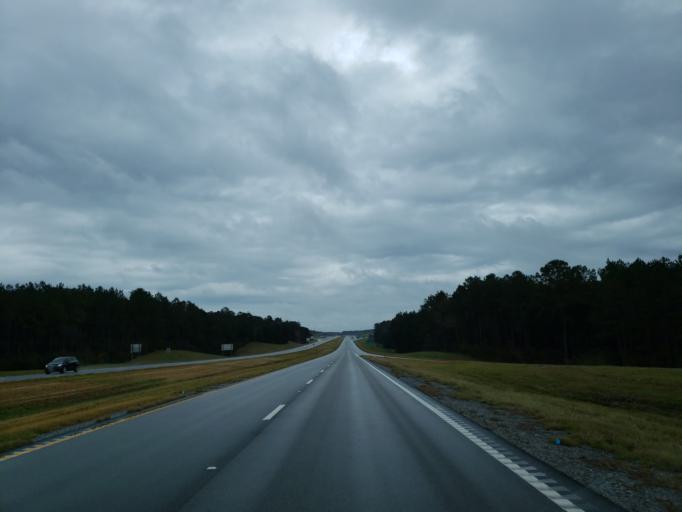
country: US
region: Mississippi
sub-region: Wayne County
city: Waynesboro
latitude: 31.7047
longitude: -88.6423
